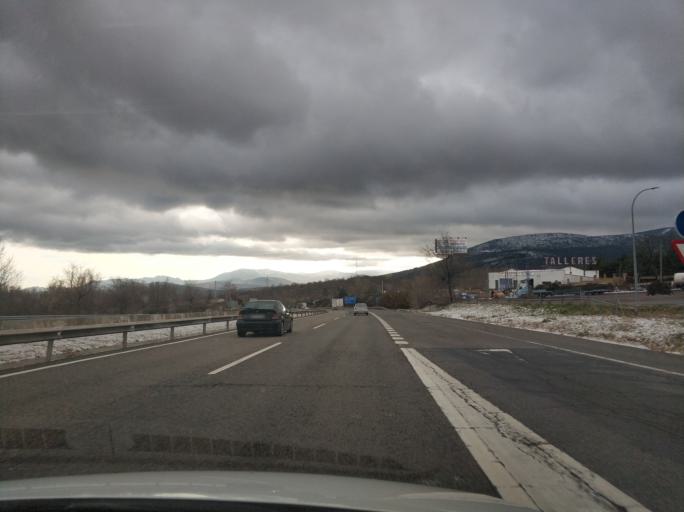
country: ES
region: Madrid
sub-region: Provincia de Madrid
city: Robregordo
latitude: 41.0964
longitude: -3.5936
